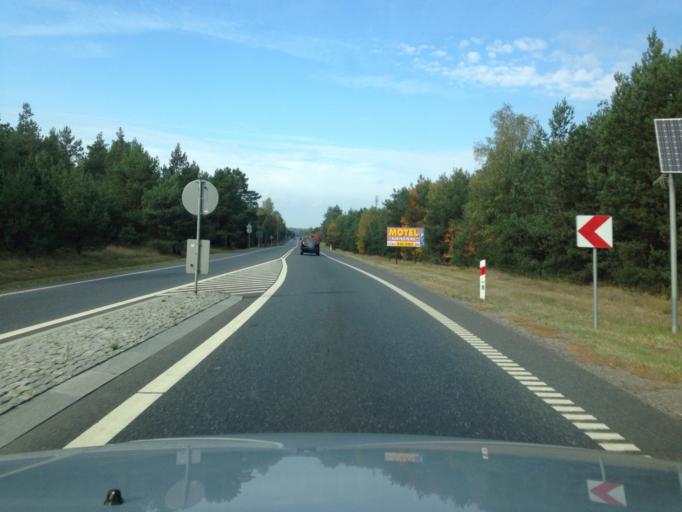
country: PL
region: Kujawsko-Pomorskie
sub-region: Grudziadz
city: Grudziadz
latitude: 53.5222
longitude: 18.6883
